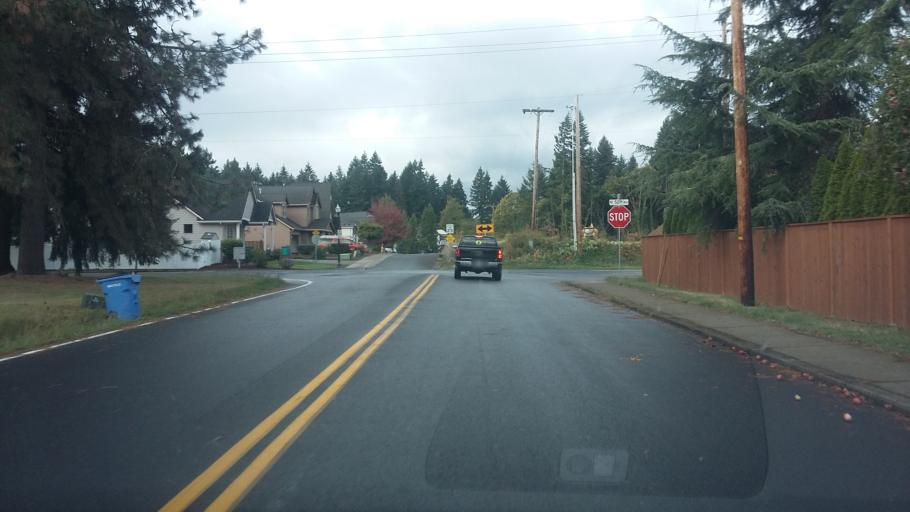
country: US
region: Washington
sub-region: Clark County
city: Barberton
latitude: 45.7005
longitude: -122.6198
